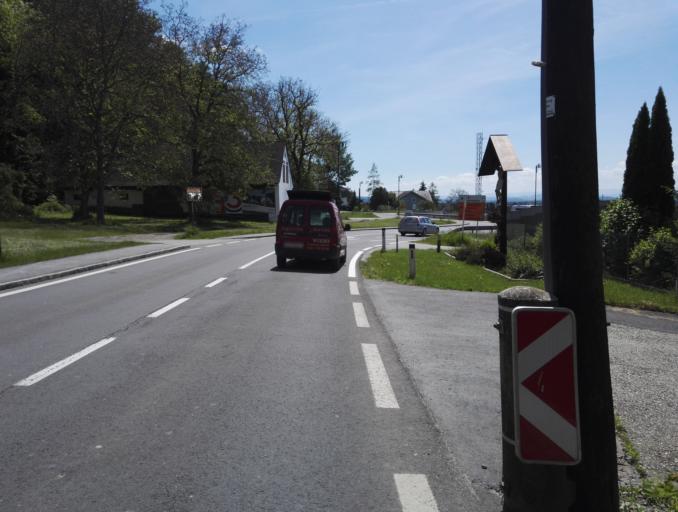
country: AT
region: Styria
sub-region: Politischer Bezirk Graz-Umgebung
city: Hausmannstatten
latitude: 47.0005
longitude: 15.5056
